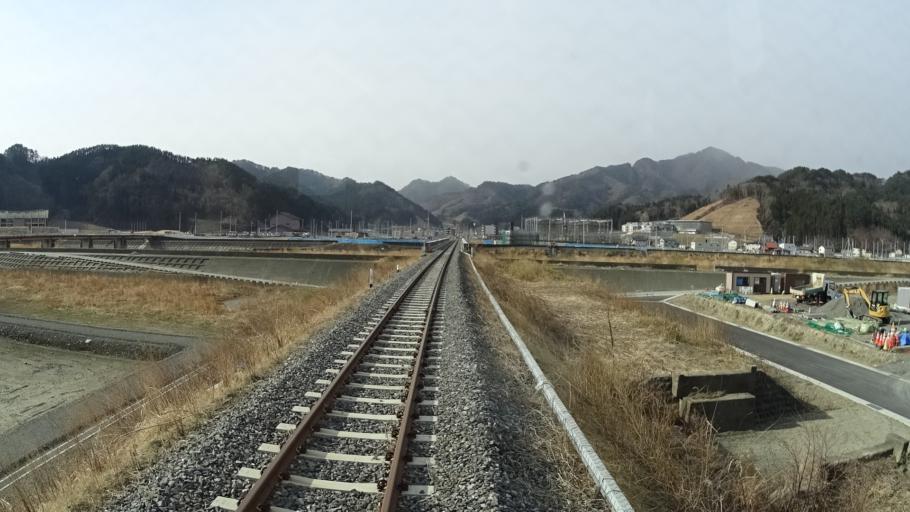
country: JP
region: Iwate
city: Otsuchi
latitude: 39.3309
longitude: 141.8900
